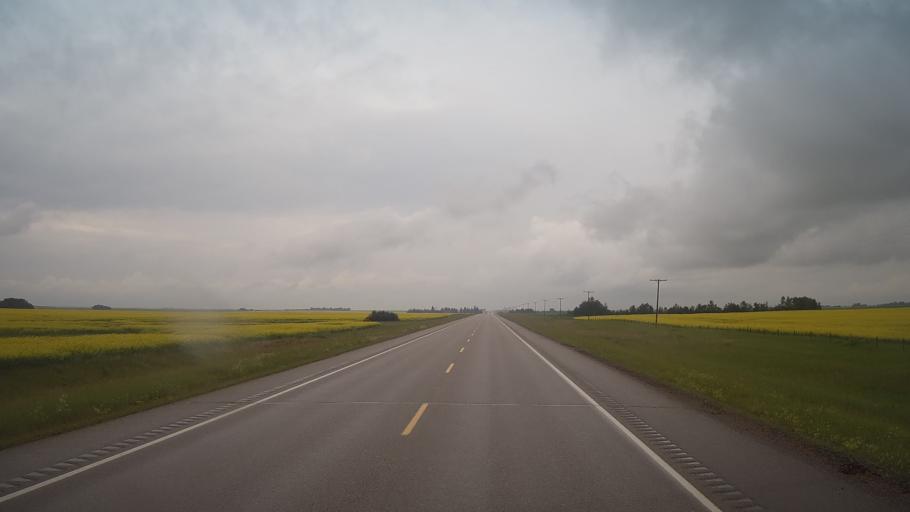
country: CA
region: Saskatchewan
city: Unity
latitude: 52.4349
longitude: -109.0074
